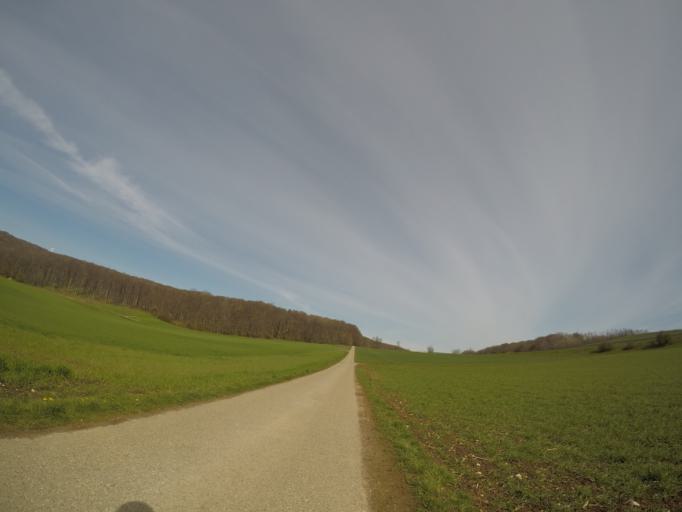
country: DE
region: Baden-Wuerttemberg
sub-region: Regierungsbezirk Stuttgart
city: Hohenstadt
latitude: 48.5339
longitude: 9.6530
